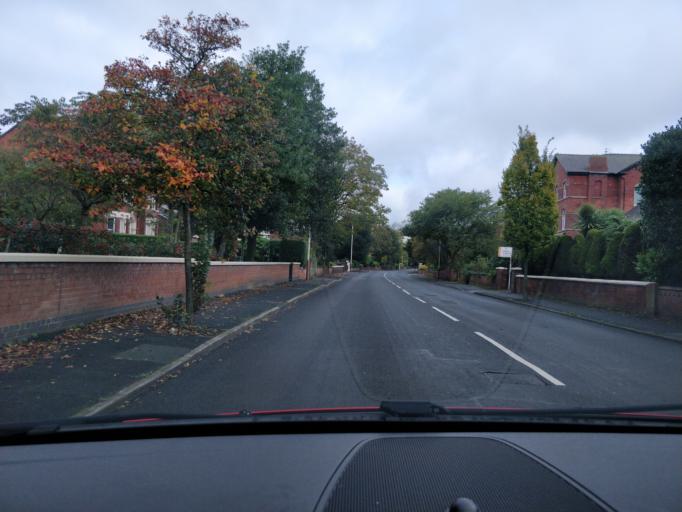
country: GB
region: England
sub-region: Sefton
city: Southport
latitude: 53.6323
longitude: -3.0249
